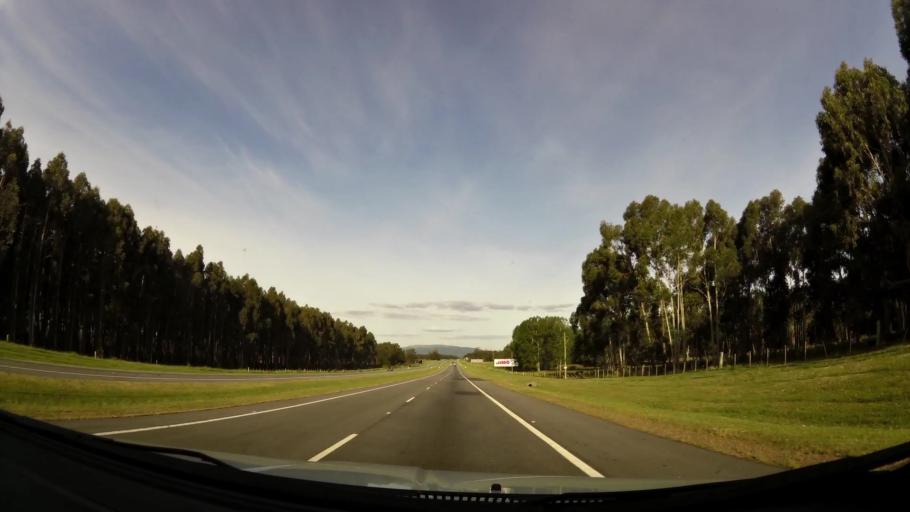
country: UY
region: Lavalleja
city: Solis de Mataojo
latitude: -34.7807
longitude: -55.4762
